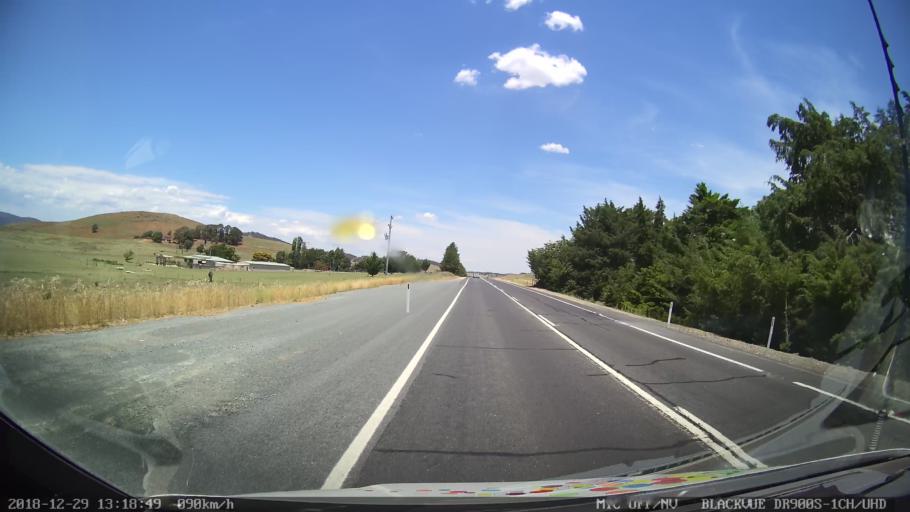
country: AU
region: Australian Capital Territory
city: Macarthur
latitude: -35.7566
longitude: 149.1611
